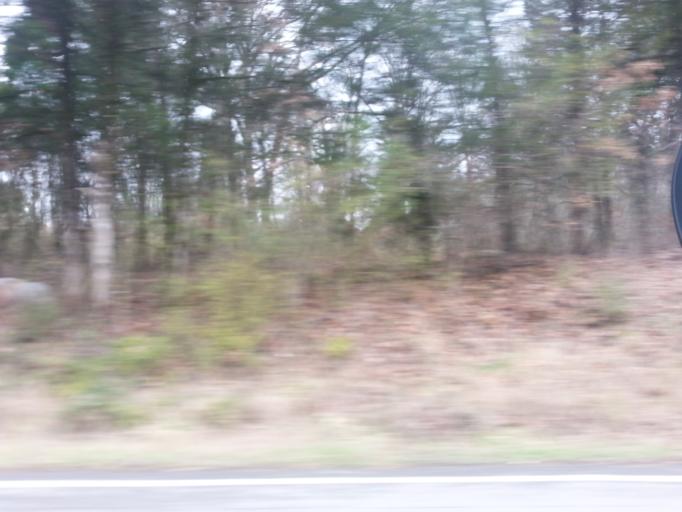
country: US
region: Tennessee
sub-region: Grainger County
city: Blaine
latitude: 36.1389
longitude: -83.6687
